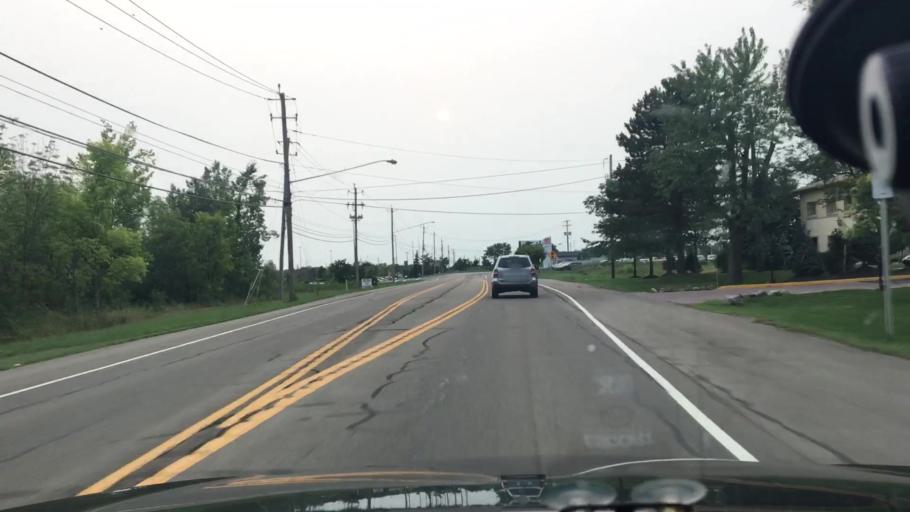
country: US
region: New York
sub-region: Erie County
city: Blasdell
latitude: 42.7692
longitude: -78.8053
